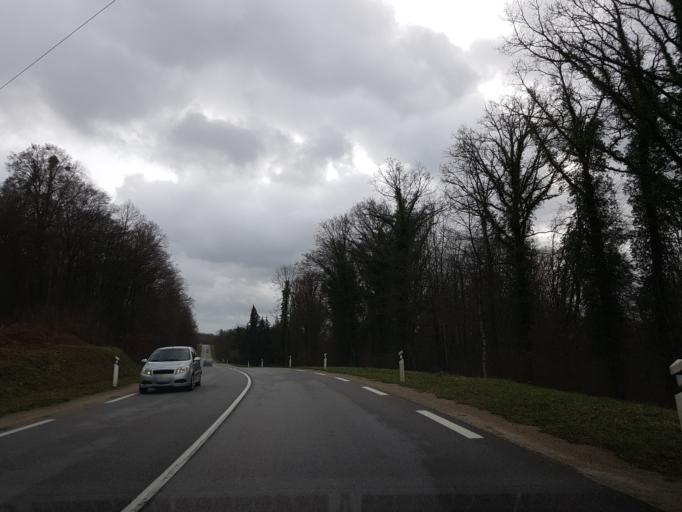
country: FR
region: Champagne-Ardenne
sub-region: Departement de la Haute-Marne
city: Fayl-Billot
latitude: 47.8031
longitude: 5.5592
